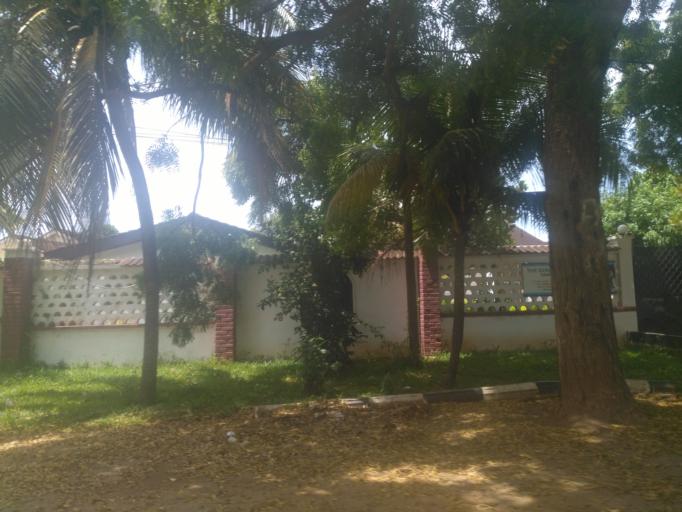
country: TZ
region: Zanzibar Urban/West
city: Zanzibar
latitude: -6.2095
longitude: 39.2106
